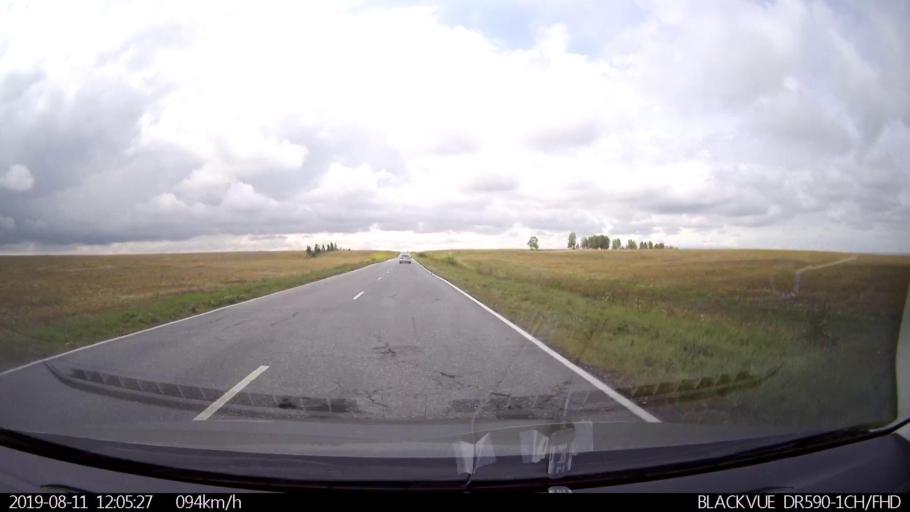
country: RU
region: Ulyanovsk
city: Silikatnyy
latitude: 53.9969
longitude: 48.1395
